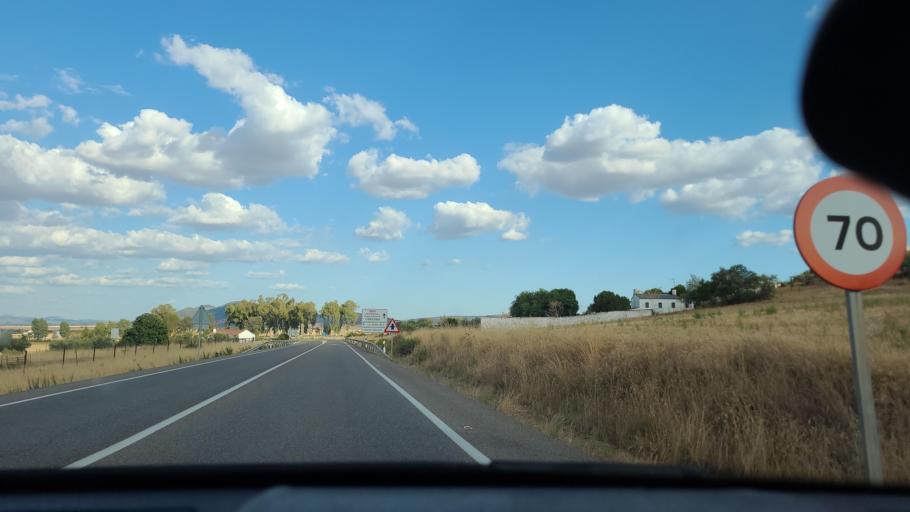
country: ES
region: Andalusia
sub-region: Province of Cordoba
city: Fuente Obejuna
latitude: 38.2750
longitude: -5.4144
